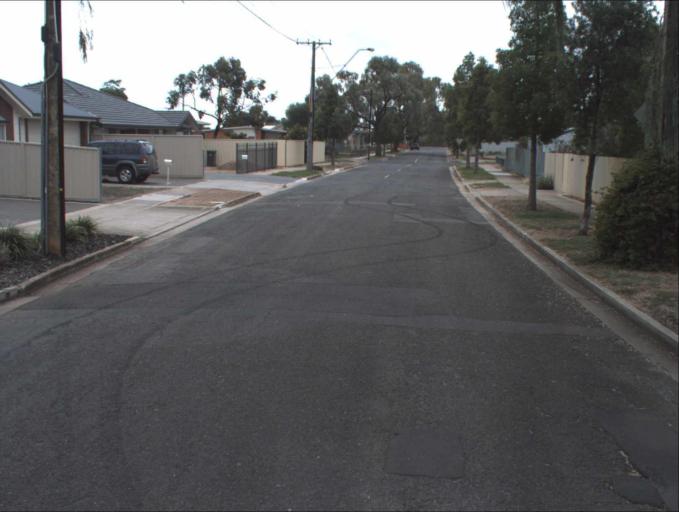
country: AU
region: South Australia
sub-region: Port Adelaide Enfield
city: Enfield
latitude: -34.8541
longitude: 138.6214
